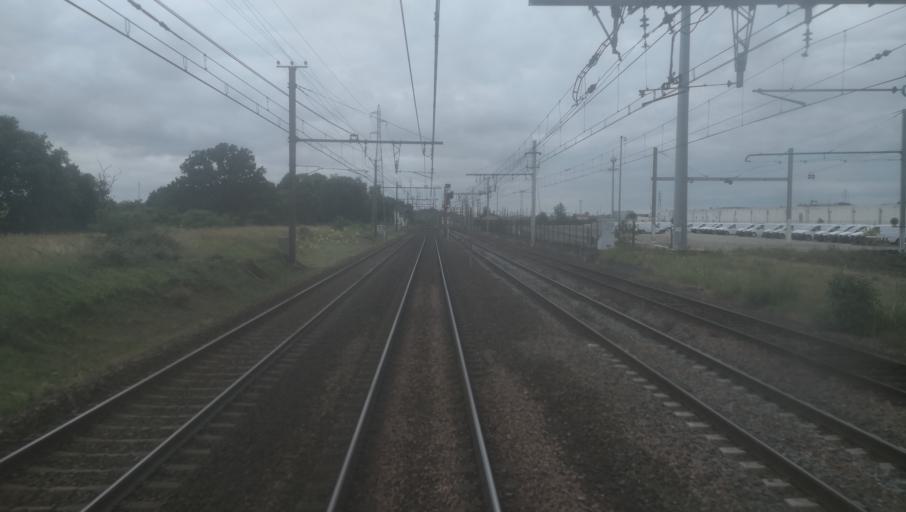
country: FR
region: Midi-Pyrenees
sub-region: Departement de la Haute-Garonne
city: Fenouillet
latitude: 43.6851
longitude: 1.4010
